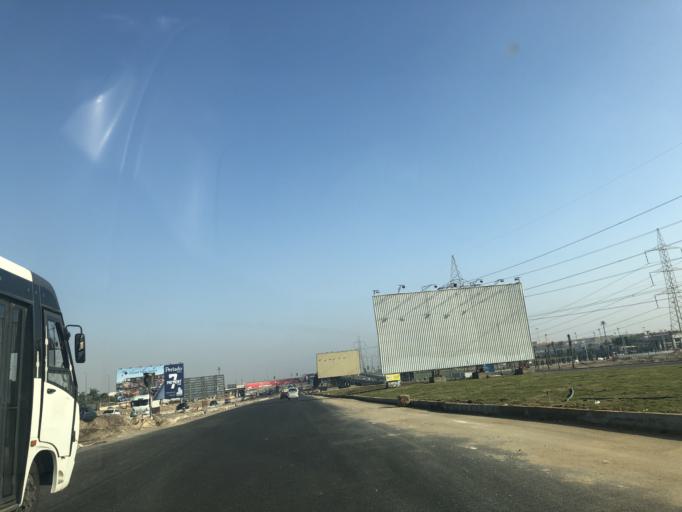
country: EG
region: Al Jizah
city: Madinat Sittah Uktubar
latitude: 29.9721
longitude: 31.0080
